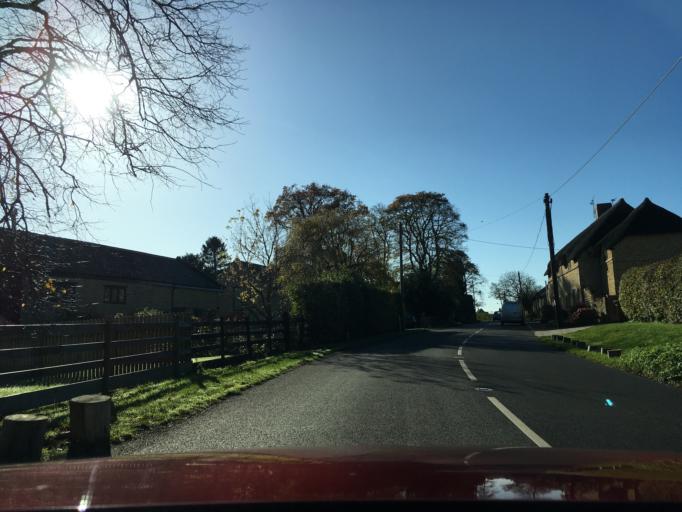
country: GB
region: England
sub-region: Somerset
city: Martock
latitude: 50.9886
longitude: -2.7651
